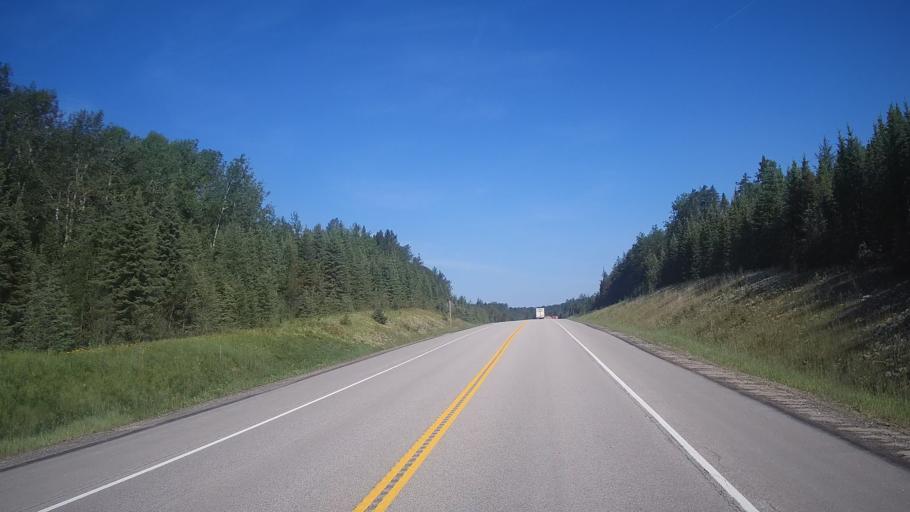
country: CA
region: Ontario
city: Dryden
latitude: 49.5683
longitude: -92.2483
